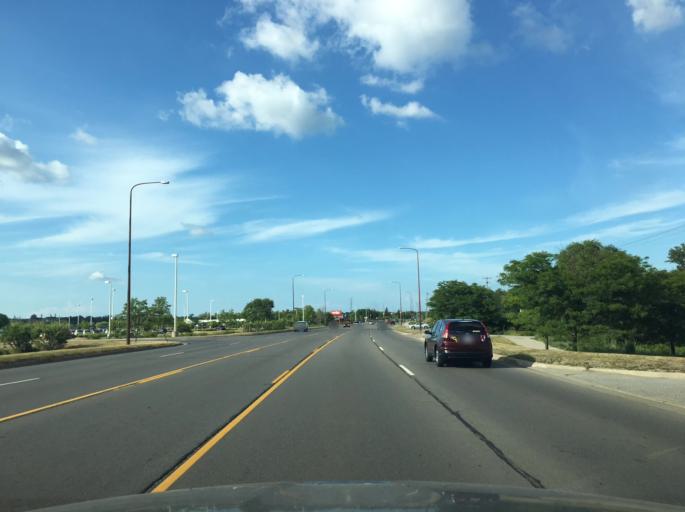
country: US
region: Michigan
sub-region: Grand Traverse County
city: Traverse City
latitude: 44.7408
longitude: -85.6435
